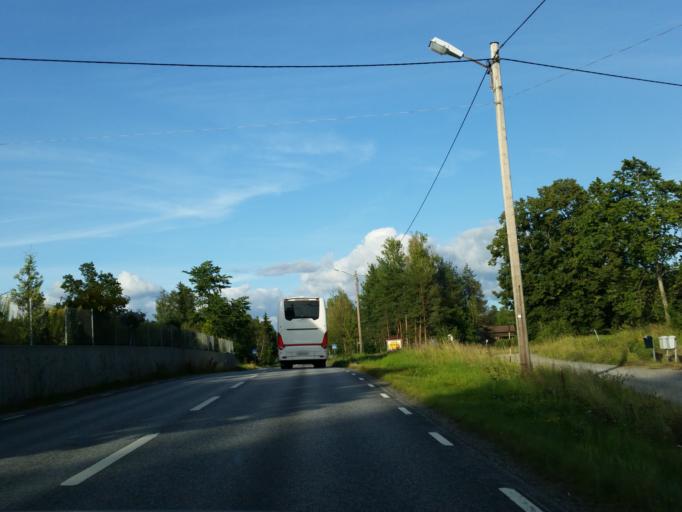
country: SE
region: Stockholm
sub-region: Sodertalje Kommun
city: Molnbo
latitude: 59.0458
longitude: 17.4130
